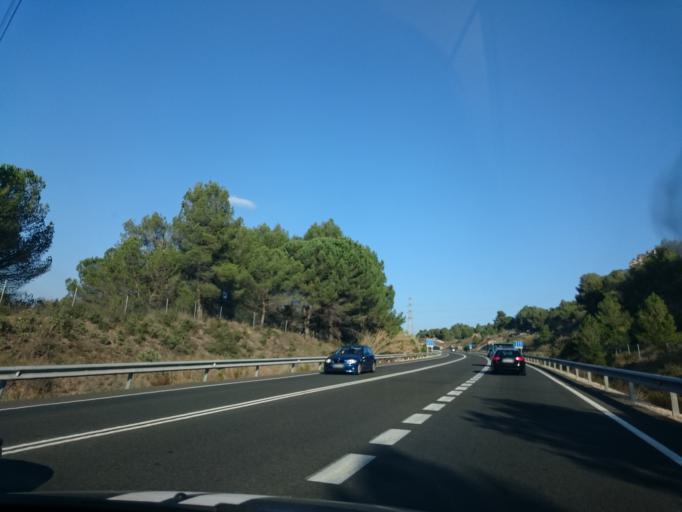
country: ES
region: Catalonia
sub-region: Provincia de Barcelona
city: La Pobla de Claramunt
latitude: 41.5614
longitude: 1.6801
